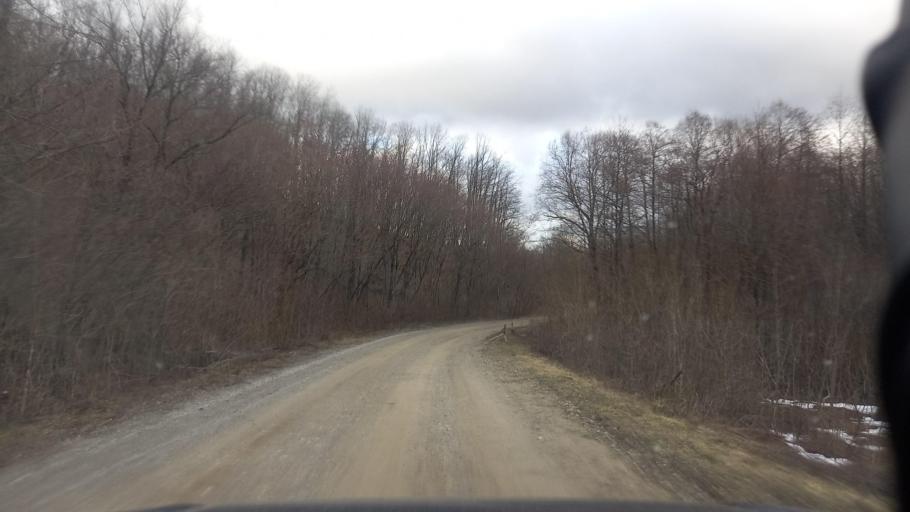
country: RU
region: Krasnodarskiy
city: Lermontovo
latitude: 44.4814
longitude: 38.7934
